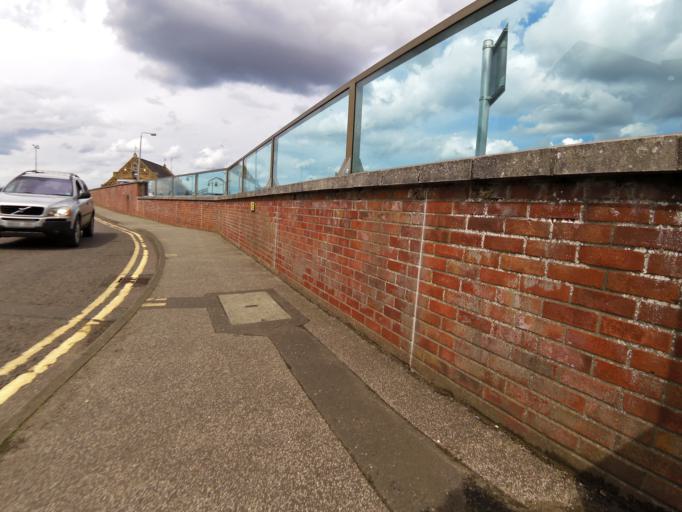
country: GB
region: England
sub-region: Norfolk
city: Wells-next-the-Sea
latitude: 52.9578
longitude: 0.8508
